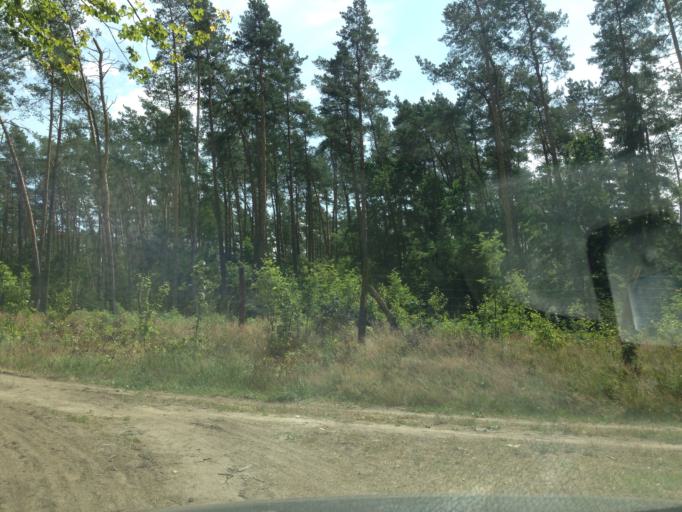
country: PL
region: Kujawsko-Pomorskie
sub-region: Powiat brodnicki
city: Bartniczka
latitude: 53.2816
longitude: 19.5655
